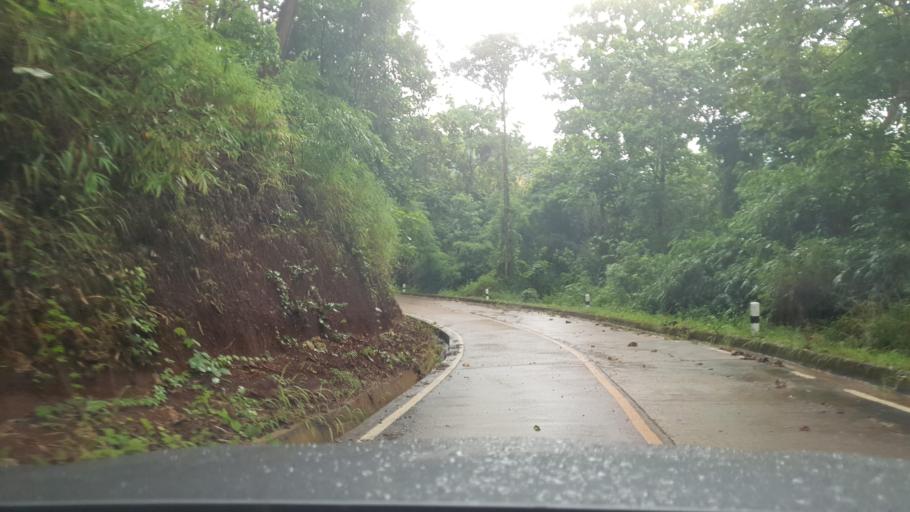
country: TH
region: Chiang Mai
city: Samoeng
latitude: 18.8386
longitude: 98.7802
